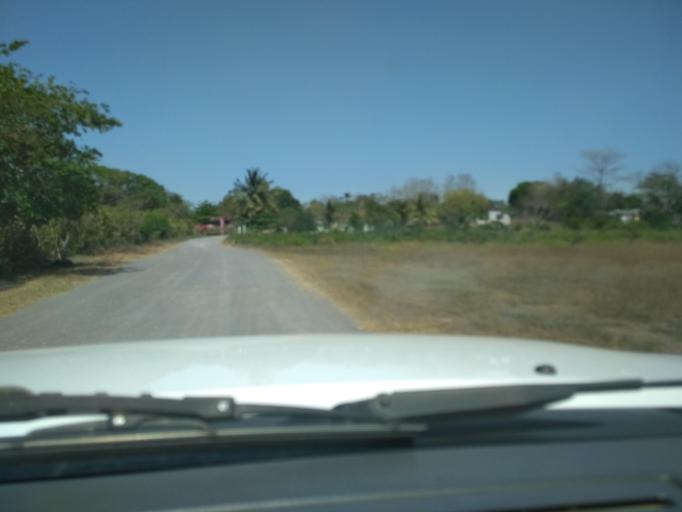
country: MX
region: Veracruz
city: Manlio Fabio Altamirano
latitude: 19.1566
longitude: -96.3307
